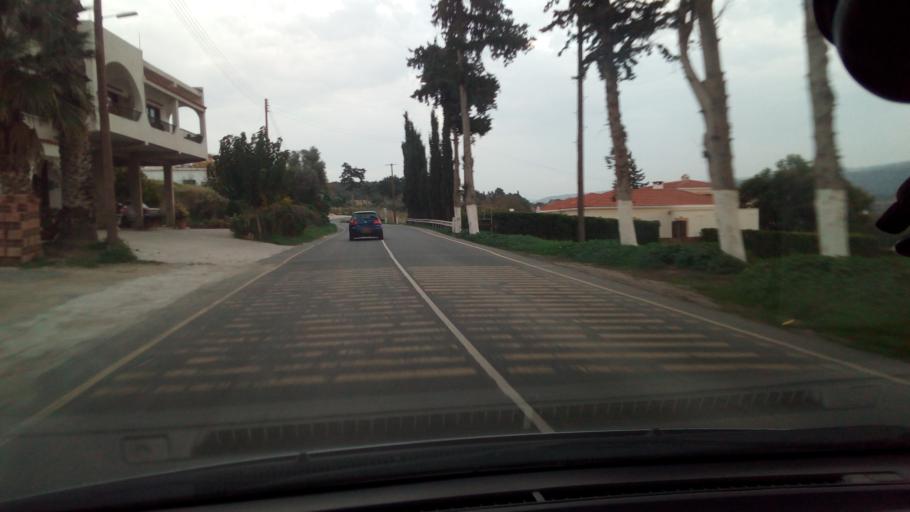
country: CY
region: Pafos
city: Polis
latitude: 35.0279
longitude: 32.4311
